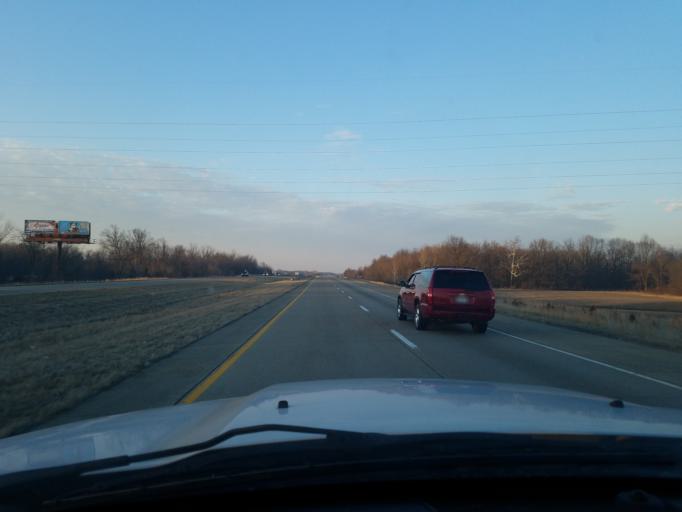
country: US
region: Indiana
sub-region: Vanderburgh County
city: Melody Hill
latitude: 38.0305
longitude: -87.4724
